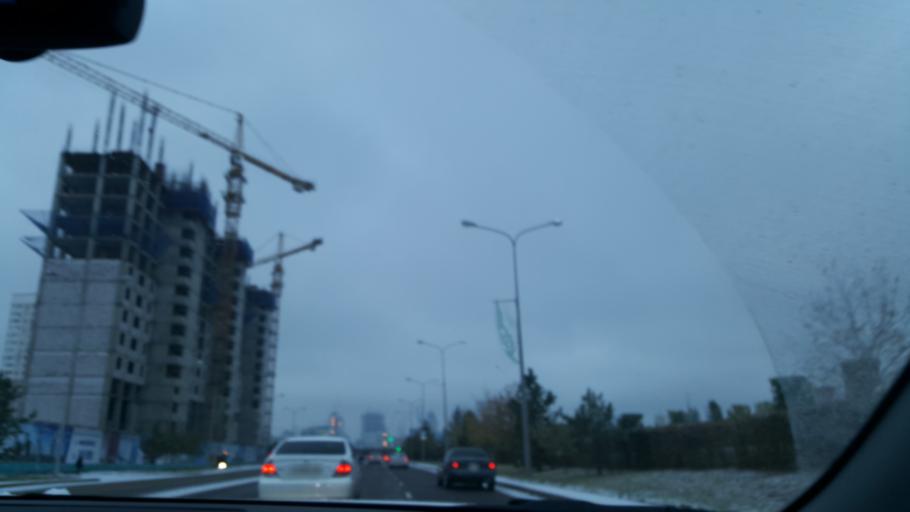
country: KZ
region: Astana Qalasy
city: Astana
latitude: 51.1205
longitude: 71.4614
